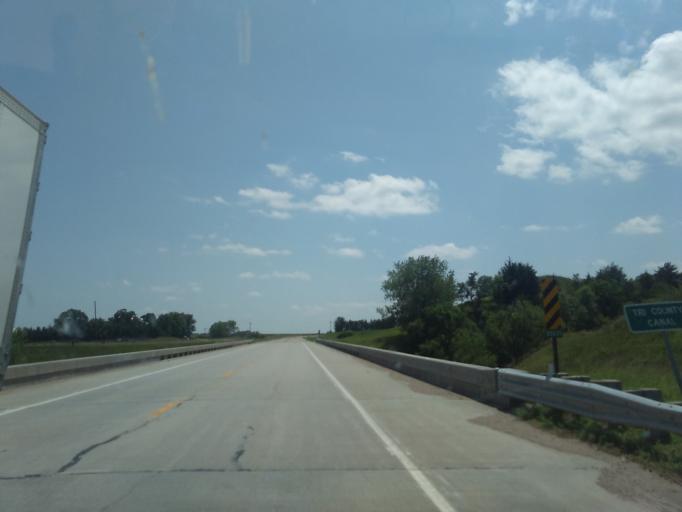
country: US
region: Nebraska
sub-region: Dawson County
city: Lexington
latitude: 40.6938
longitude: -99.7945
